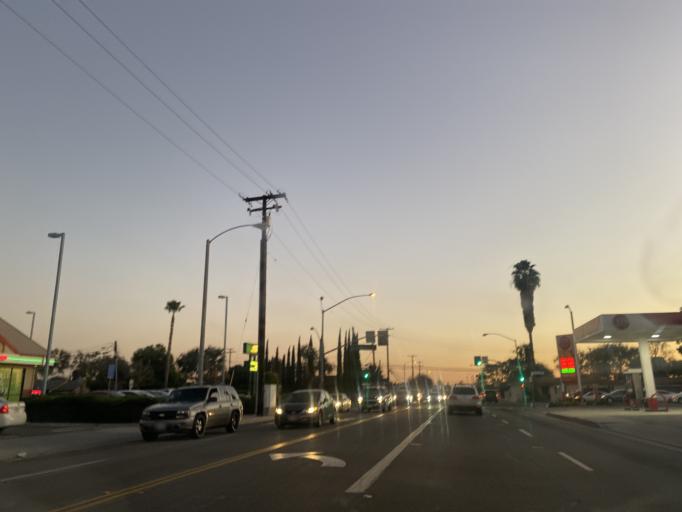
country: US
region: California
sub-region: Orange County
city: Fullerton
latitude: 33.8711
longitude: -117.9070
